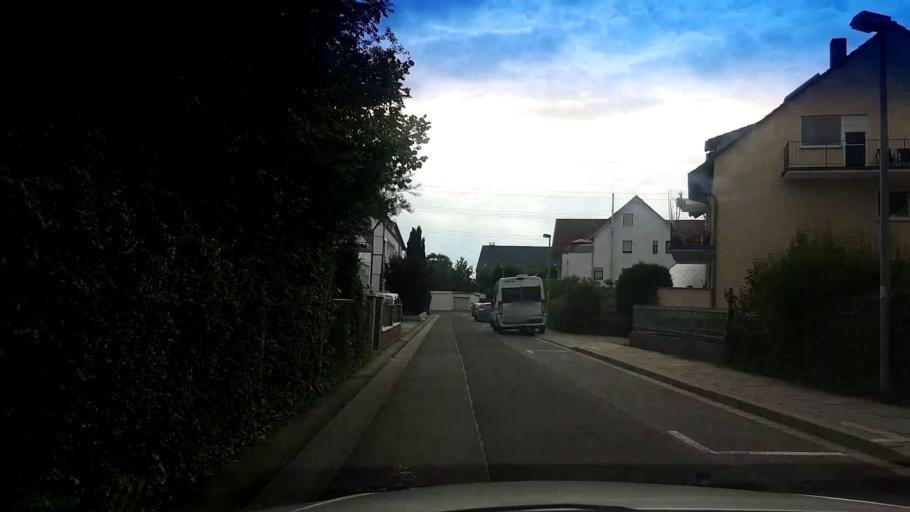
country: DE
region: Bavaria
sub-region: Upper Franconia
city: Bamberg
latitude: 49.9042
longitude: 10.9219
